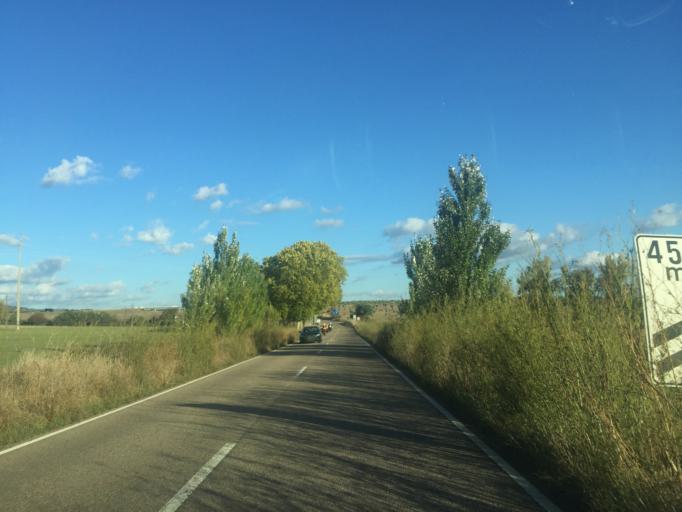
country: PT
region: Portalegre
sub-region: Alter do Chao
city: Alter do Chao
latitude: 39.1973
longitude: -7.7057
